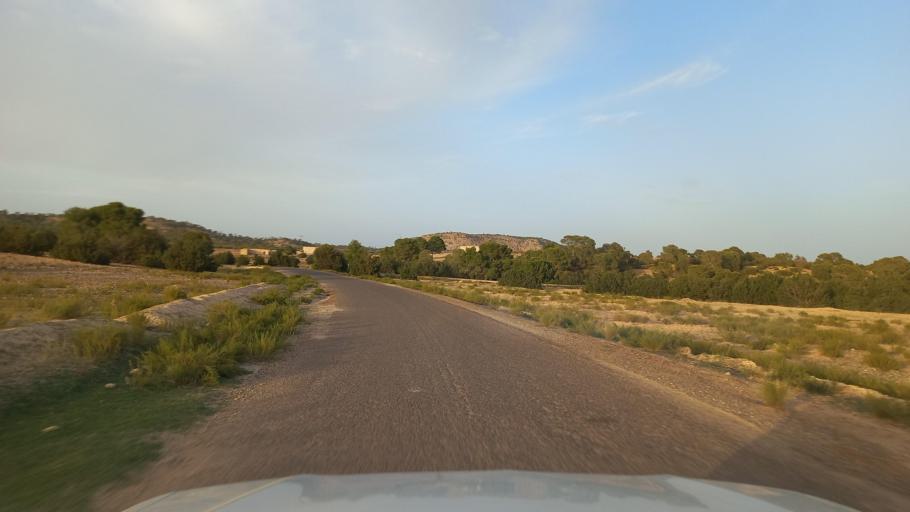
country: TN
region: Al Qasrayn
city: Sbiba
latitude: 35.4112
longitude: 8.9260
